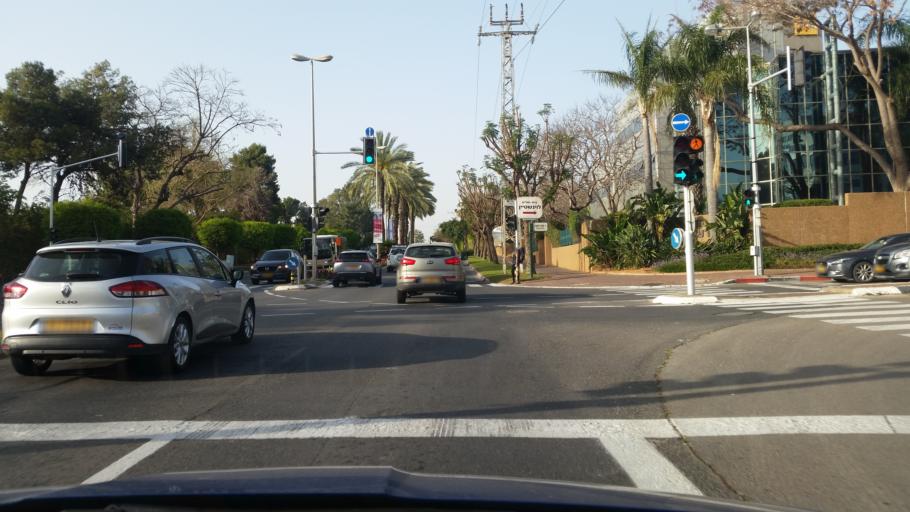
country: IL
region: Central District
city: Ra'anana
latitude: 32.1873
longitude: 34.8546
